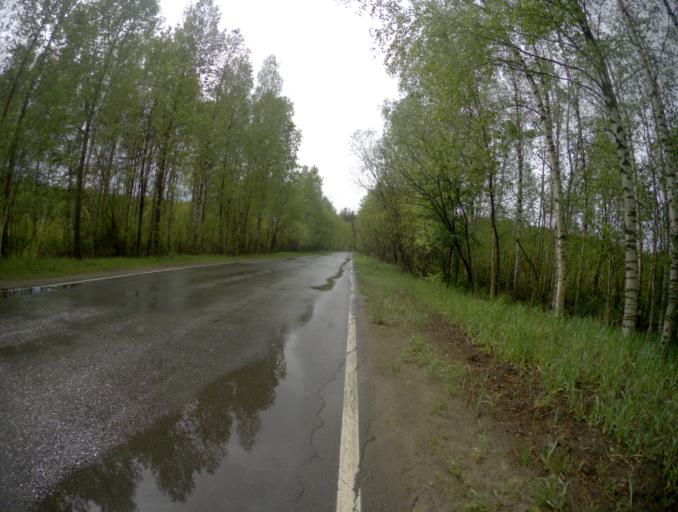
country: RU
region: Vladimir
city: Velikodvorskiy
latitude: 55.3734
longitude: 40.7922
